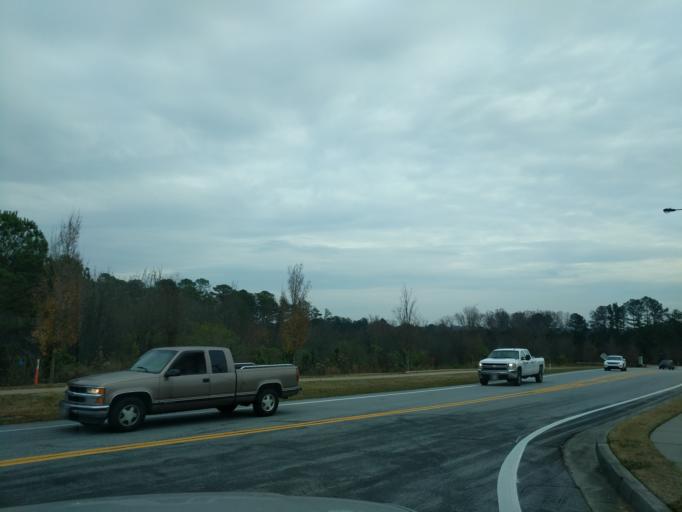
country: US
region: Georgia
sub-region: Gwinnett County
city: Duluth
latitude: 33.9825
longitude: -84.1004
